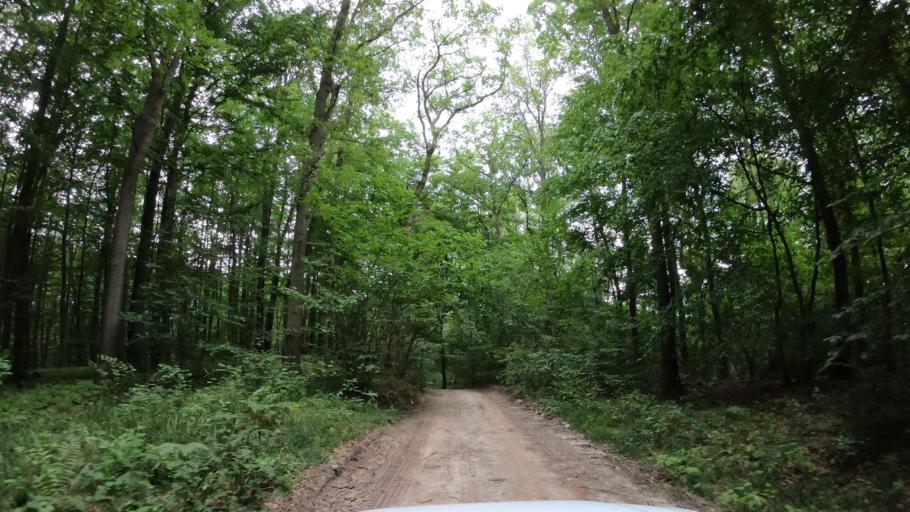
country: PL
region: West Pomeranian Voivodeship
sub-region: Powiat stargardzki
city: Dolice
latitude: 53.1989
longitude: 15.2731
